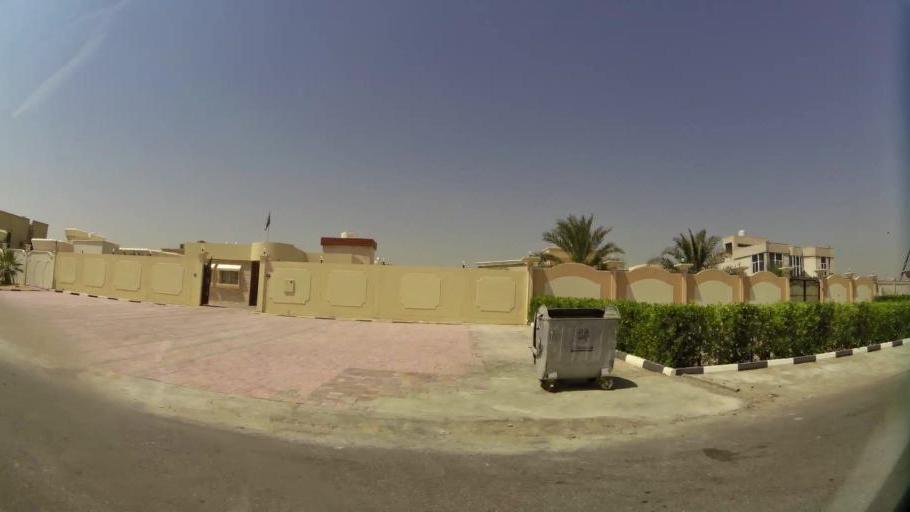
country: AE
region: Ajman
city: Ajman
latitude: 25.4200
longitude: 55.5201
